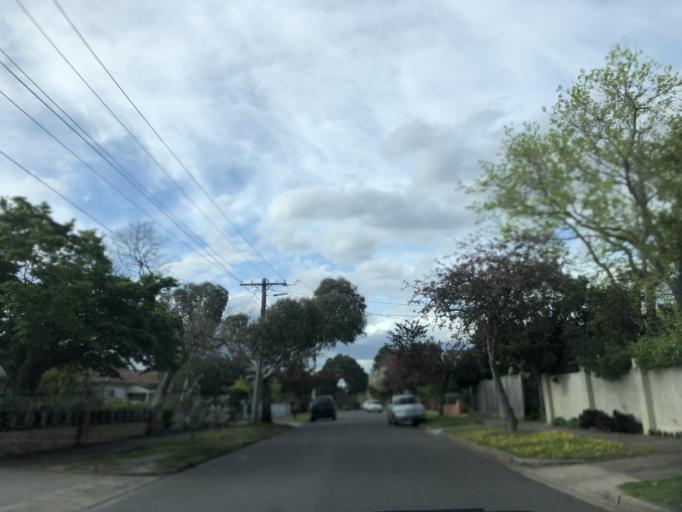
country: AU
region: Victoria
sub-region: Monash
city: Oakleigh South
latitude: -37.9234
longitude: 145.0883
